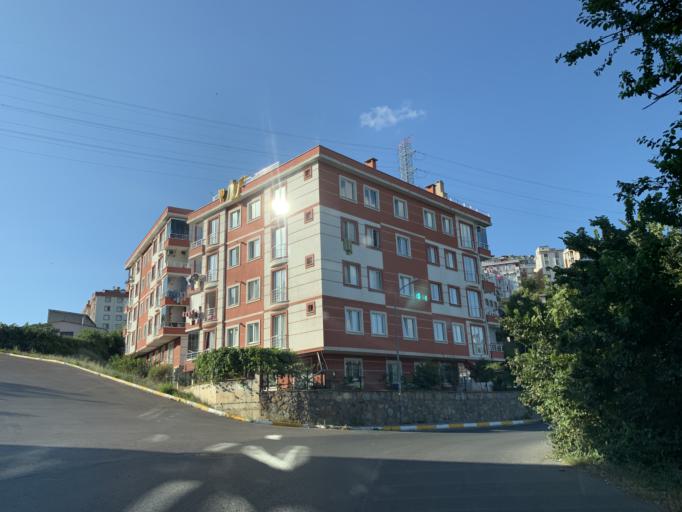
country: TR
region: Istanbul
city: Pendik
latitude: 40.9013
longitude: 29.2562
